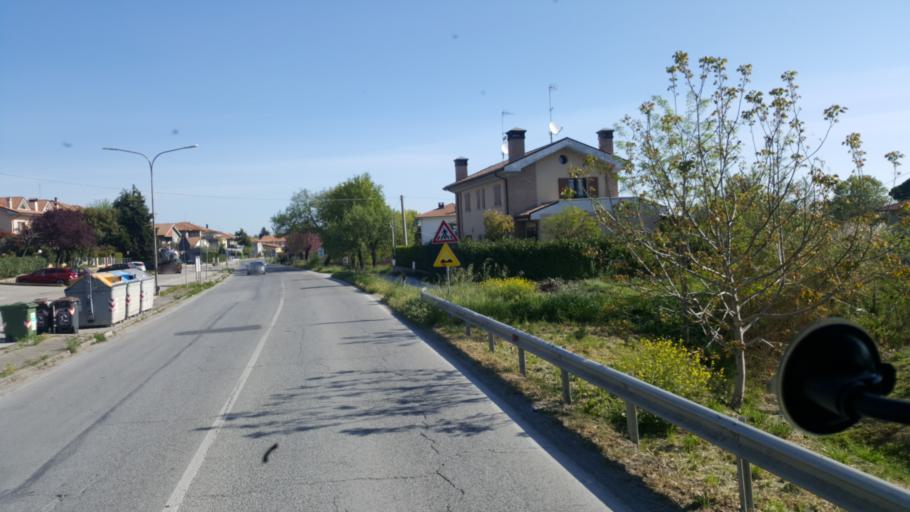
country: IT
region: Emilia-Romagna
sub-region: Provincia di Rimini
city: Sant'Andrea
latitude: 44.0300
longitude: 12.4179
